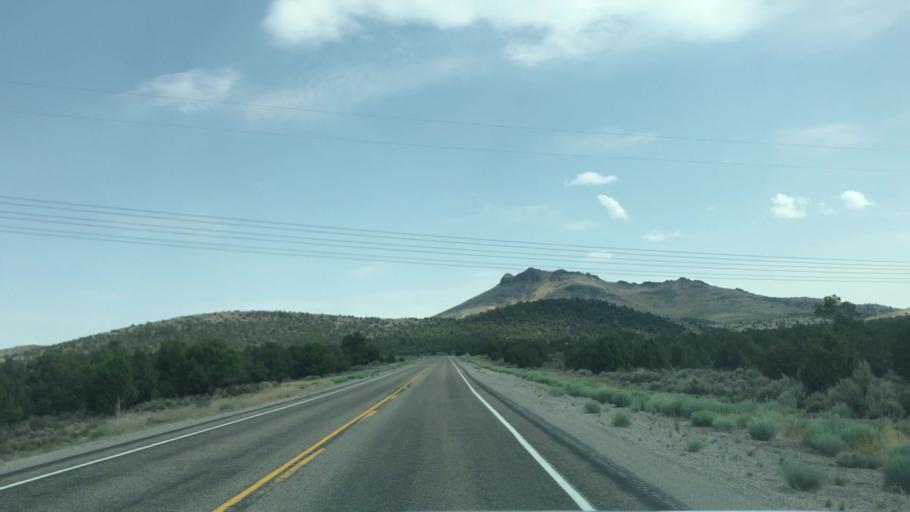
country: US
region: Nevada
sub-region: White Pine County
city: Ely
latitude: 39.4040
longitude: -115.0816
